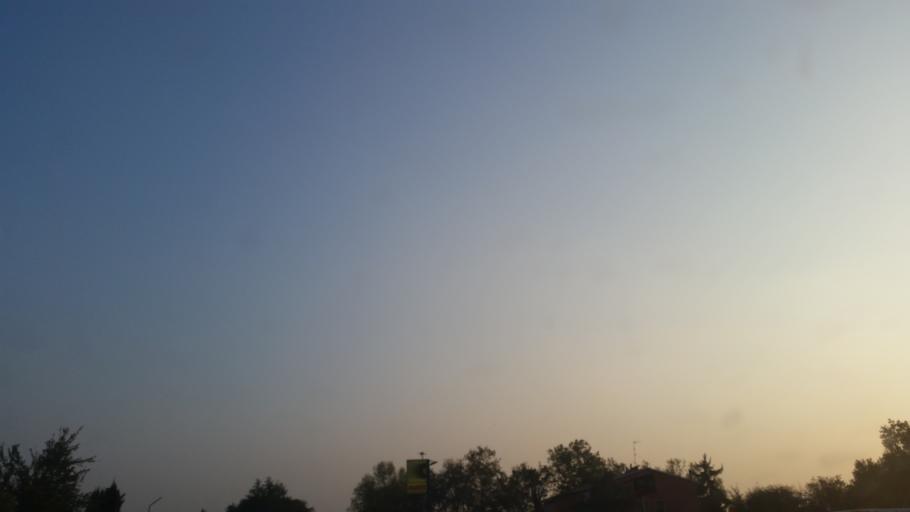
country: IT
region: Lombardy
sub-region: Provincia di Brescia
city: Bagnolo Mella
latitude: 45.4448
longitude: 10.1950
